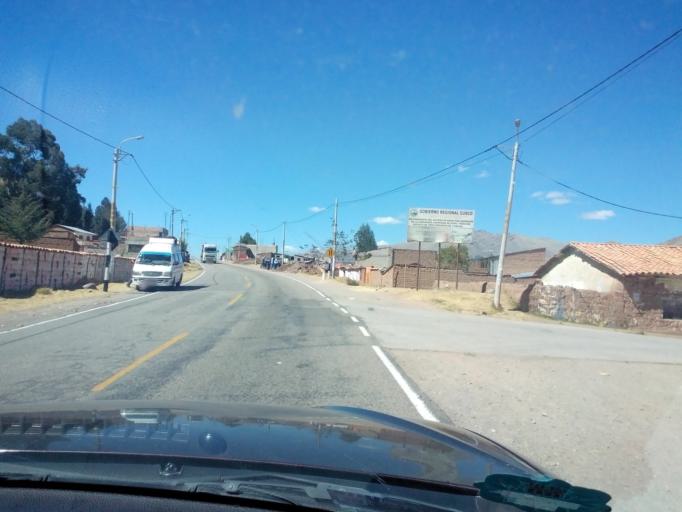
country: PE
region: Cusco
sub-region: Provincia de Canchis
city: Tinta
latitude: -14.1409
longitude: -71.4023
